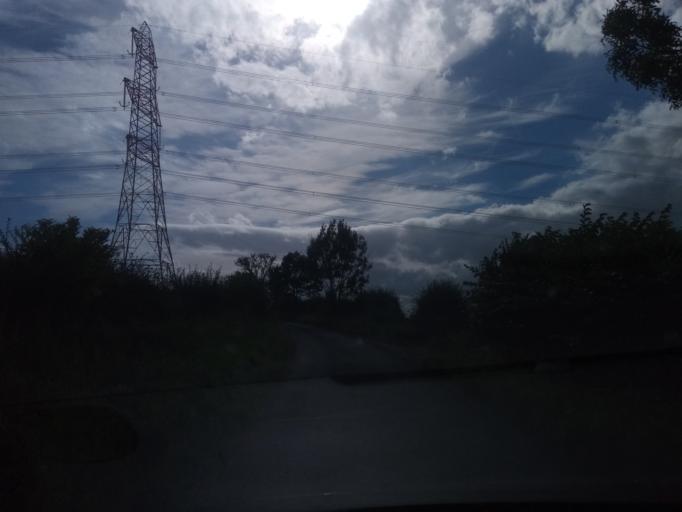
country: GB
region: Scotland
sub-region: The Scottish Borders
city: Coldstream
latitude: 55.6257
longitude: -2.1872
